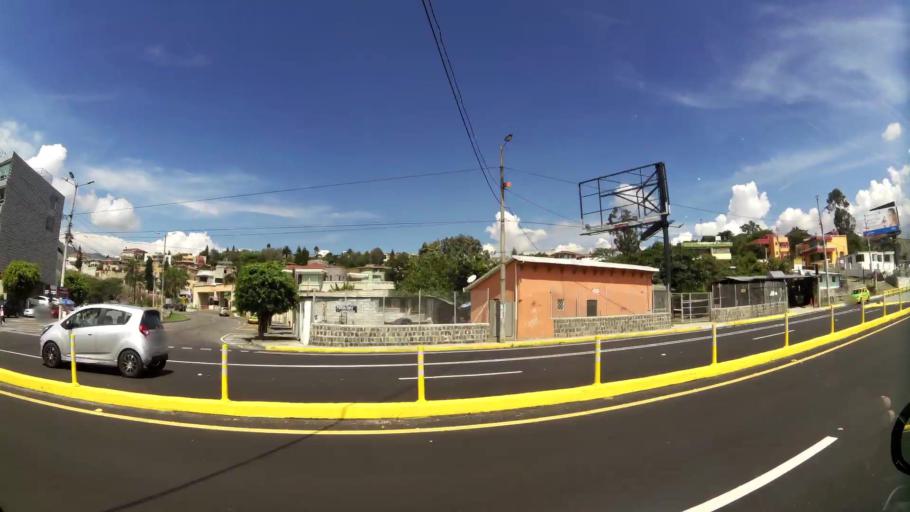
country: EC
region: Pichincha
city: Quito
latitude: -0.2061
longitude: -78.4289
